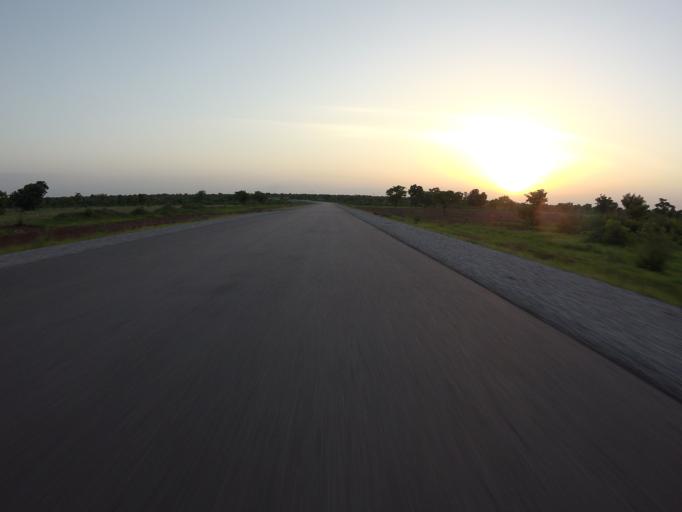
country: GH
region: Northern
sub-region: Yendi
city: Yendi
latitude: 9.9386
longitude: -0.1740
